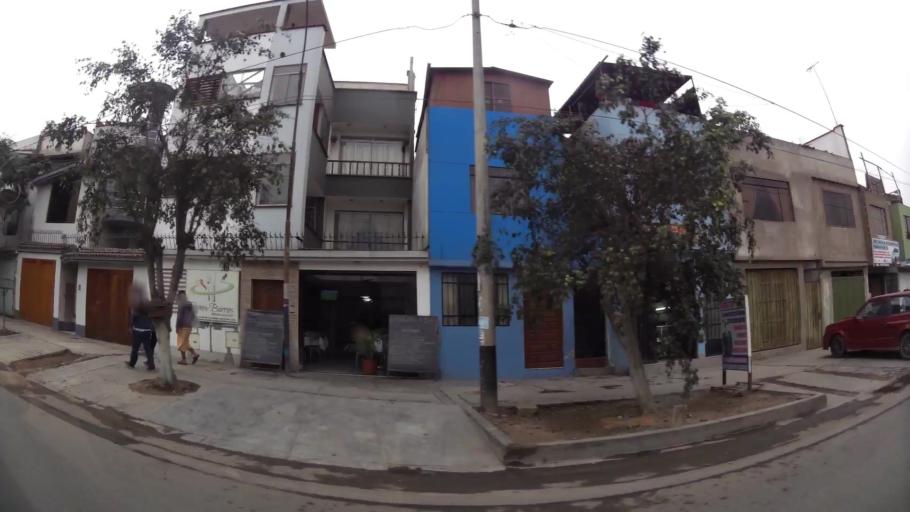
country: PE
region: Lima
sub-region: Lima
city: Vitarte
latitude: -12.0336
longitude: -76.9361
